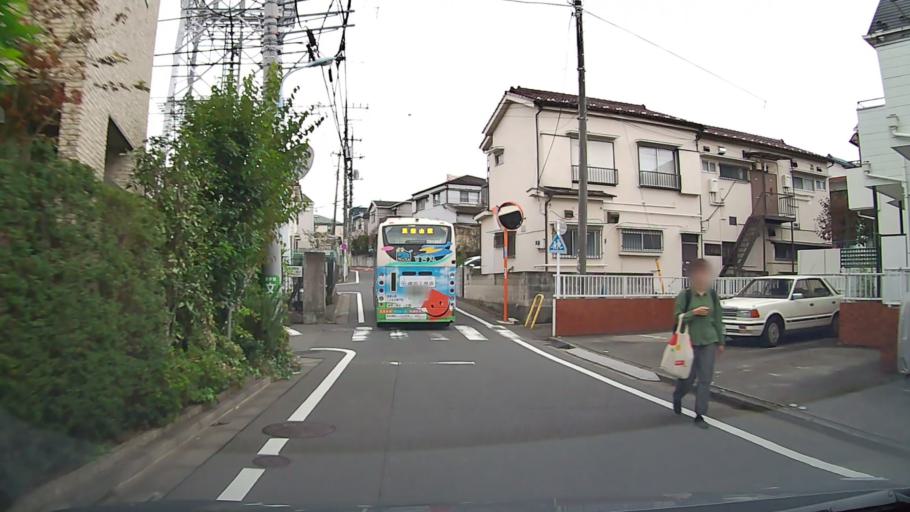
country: JP
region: Tokyo
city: Tokyo
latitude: 35.6885
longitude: 139.6303
